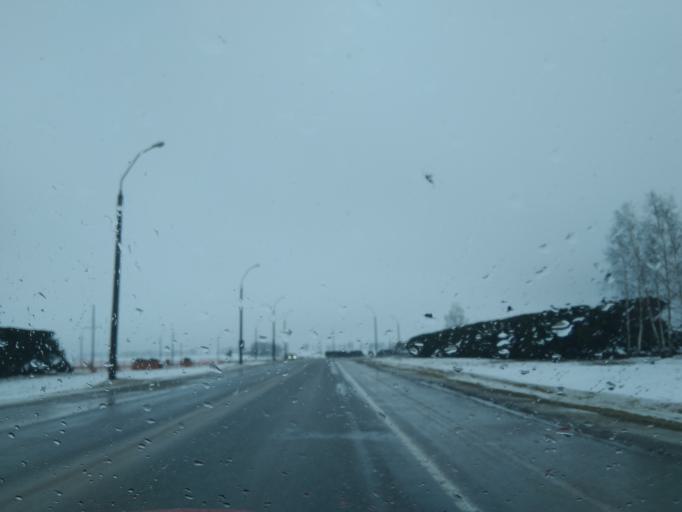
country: BY
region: Minsk
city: Nyasvizh
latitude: 53.2377
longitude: 26.6369
